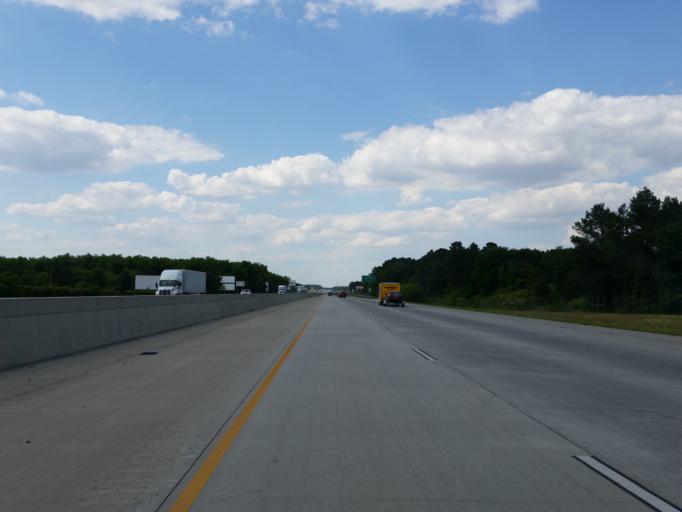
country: US
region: Georgia
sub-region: Crisp County
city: Cordele
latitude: 31.9823
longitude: -83.7550
